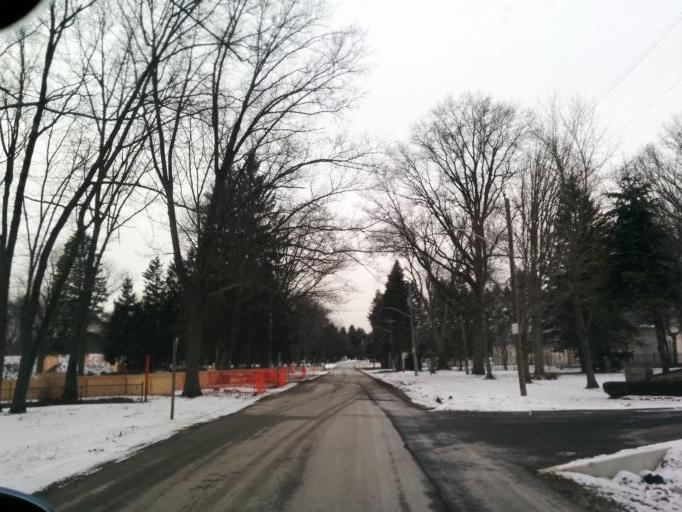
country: CA
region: Ontario
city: Mississauga
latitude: 43.5408
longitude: -79.6417
